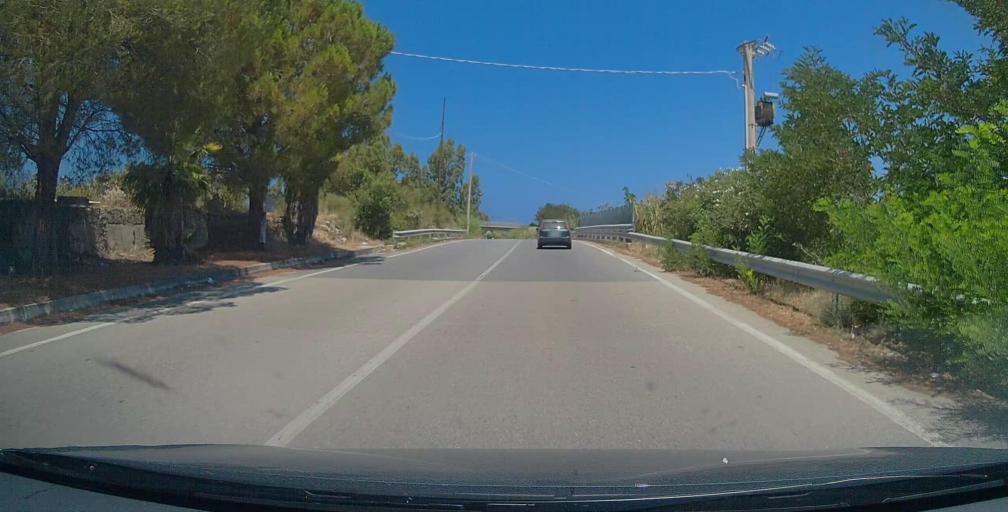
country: IT
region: Sicily
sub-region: Messina
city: Patti
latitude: 38.1405
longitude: 14.9969
